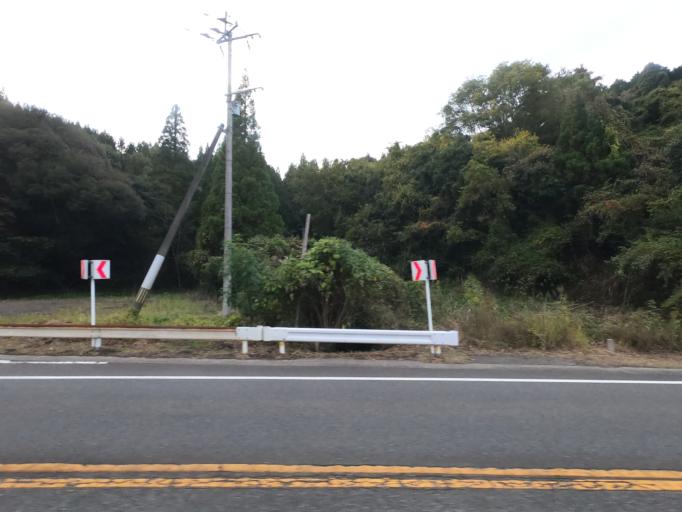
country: JP
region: Kumamoto
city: Minamata
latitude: 32.2523
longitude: 130.5033
